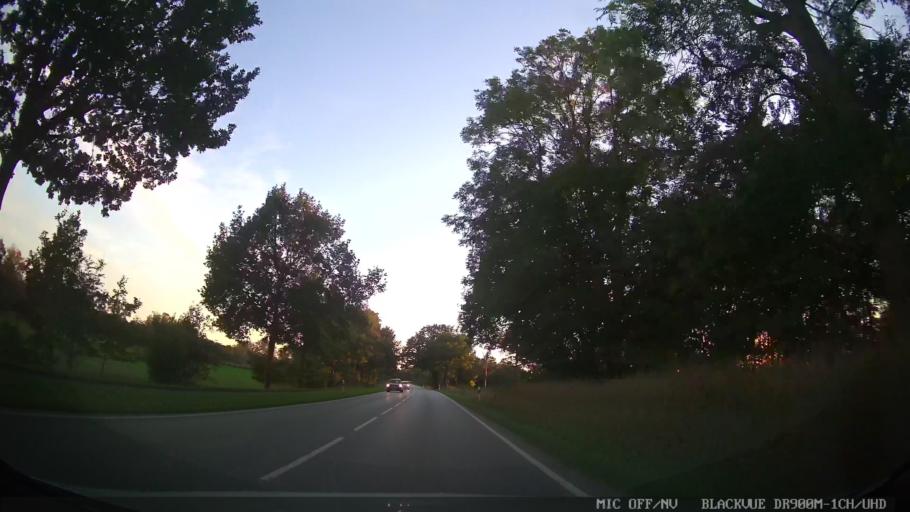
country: DE
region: Schleswig-Holstein
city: Susel
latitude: 54.0781
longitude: 10.6920
